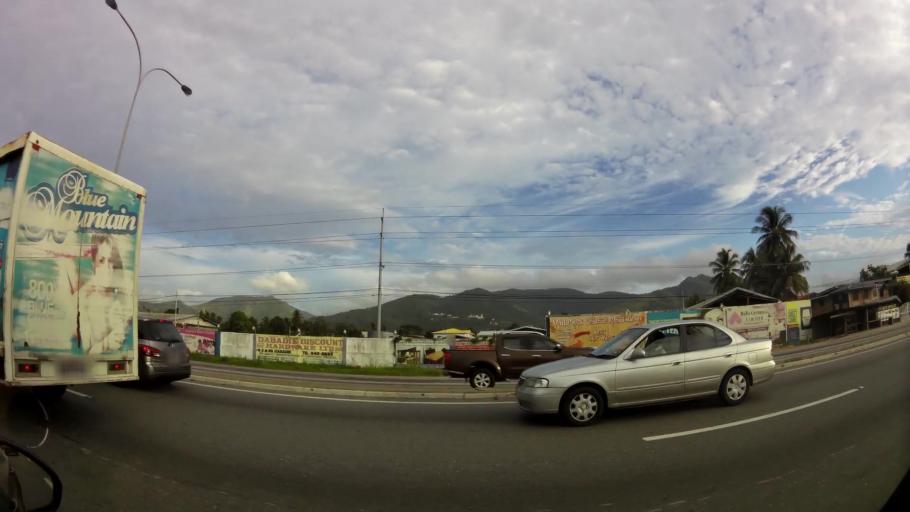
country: TT
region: Tunapuna/Piarco
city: Tunapuna
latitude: 10.6371
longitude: -61.3924
